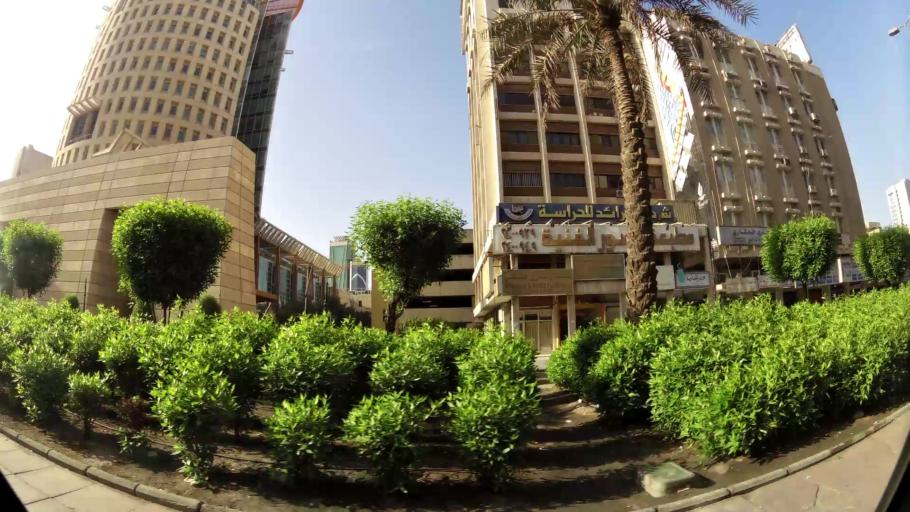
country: KW
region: Al Asimah
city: Kuwait City
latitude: 29.3729
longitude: 47.9815
